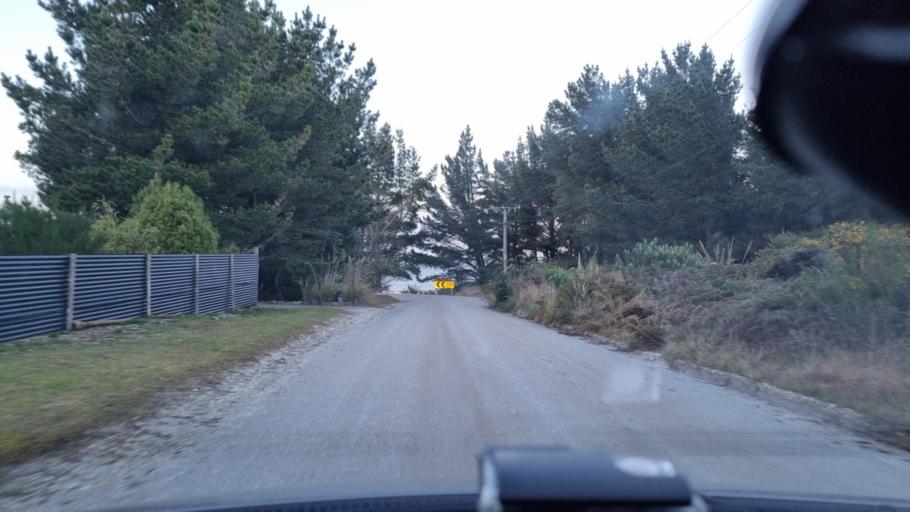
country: NZ
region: Southland
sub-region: Invercargill City
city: Bluff
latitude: -46.5594
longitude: 168.4336
